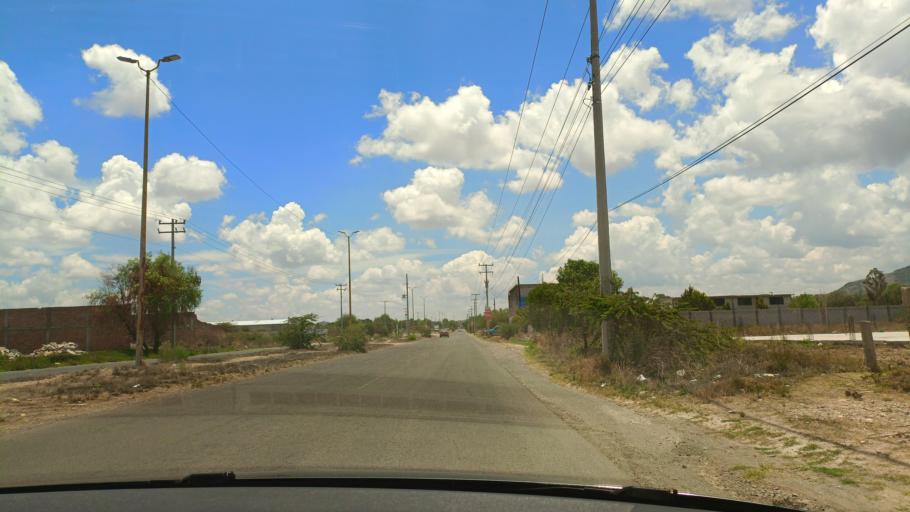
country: MX
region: Guanajuato
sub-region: San Luis de la Paz
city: San Ignacio
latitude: 21.2875
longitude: -100.5500
